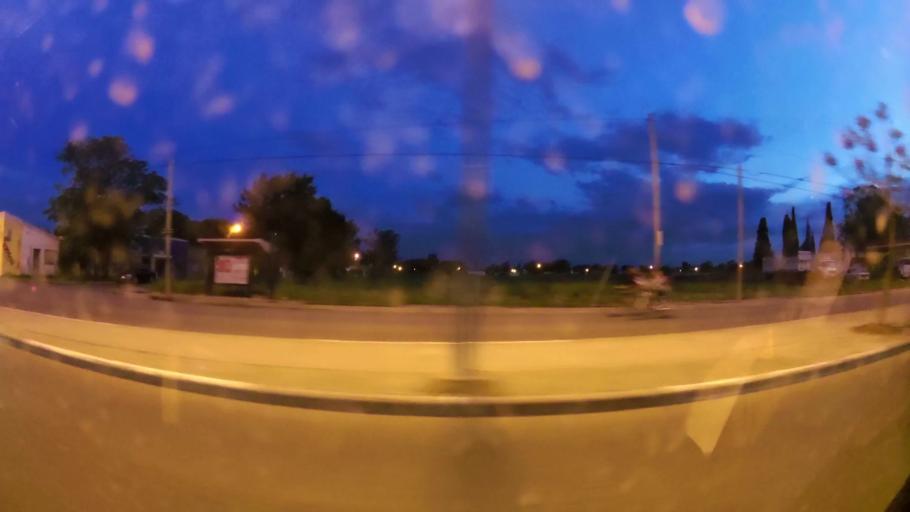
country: AR
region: Buenos Aires
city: San Nicolas de los Arroyos
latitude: -33.3544
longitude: -60.2428
